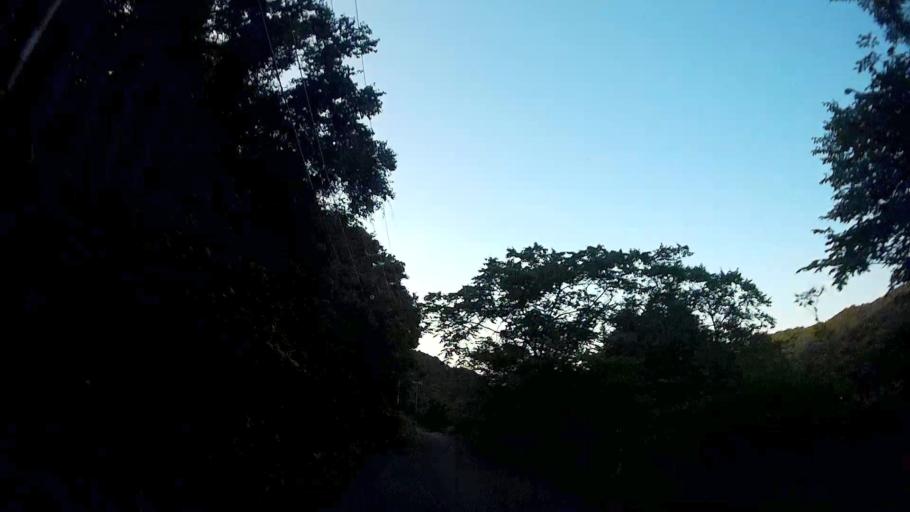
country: JP
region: Hokkaido
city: Iwanai
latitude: 42.6686
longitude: 140.0199
